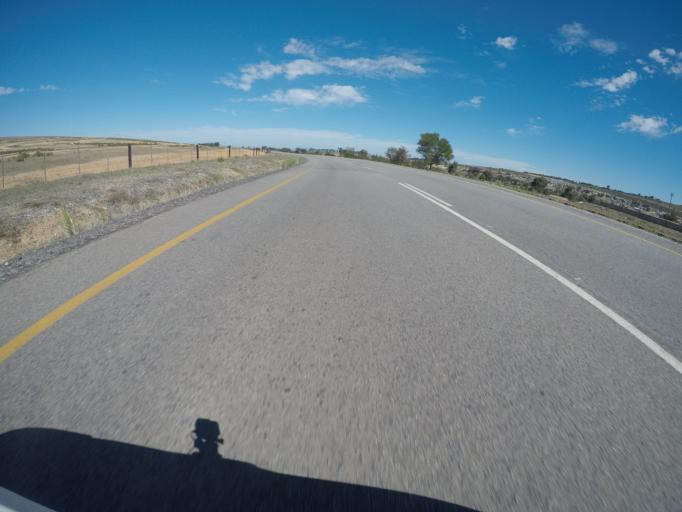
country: ZA
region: Western Cape
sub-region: West Coast District Municipality
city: Malmesbury
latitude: -33.4932
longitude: 18.6822
